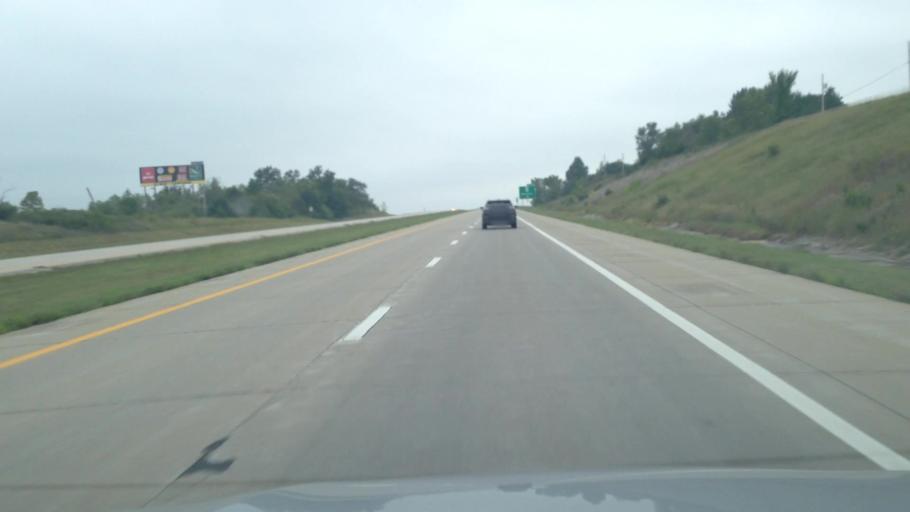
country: US
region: Missouri
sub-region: Harrison County
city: Bethany
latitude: 40.2876
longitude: -94.0125
